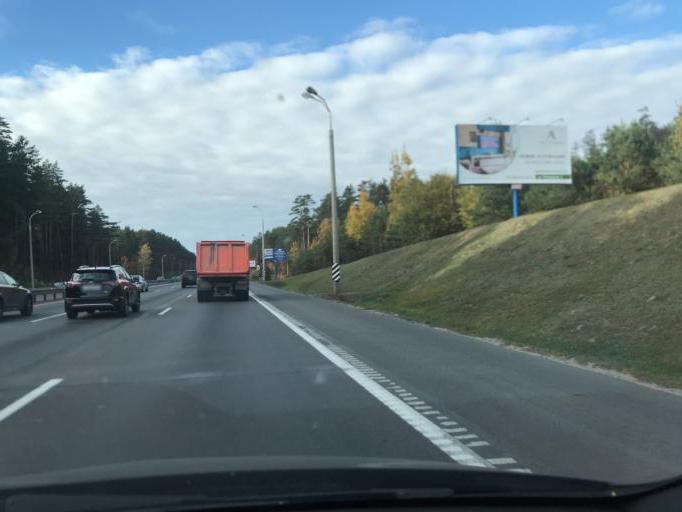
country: BY
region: Minsk
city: Borovlyany
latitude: 53.9511
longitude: 27.6517
